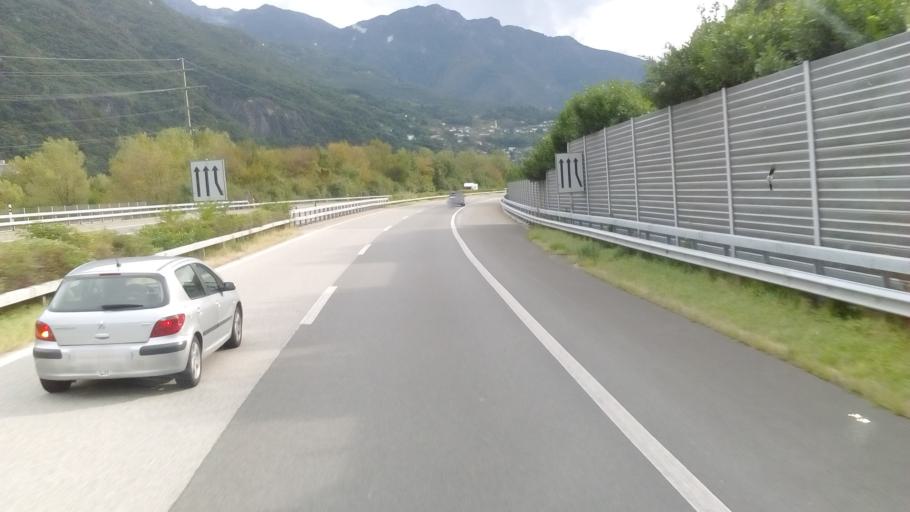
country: CH
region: Ticino
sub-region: Bellinzona District
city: Bellinzona
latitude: 46.2159
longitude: 9.0367
